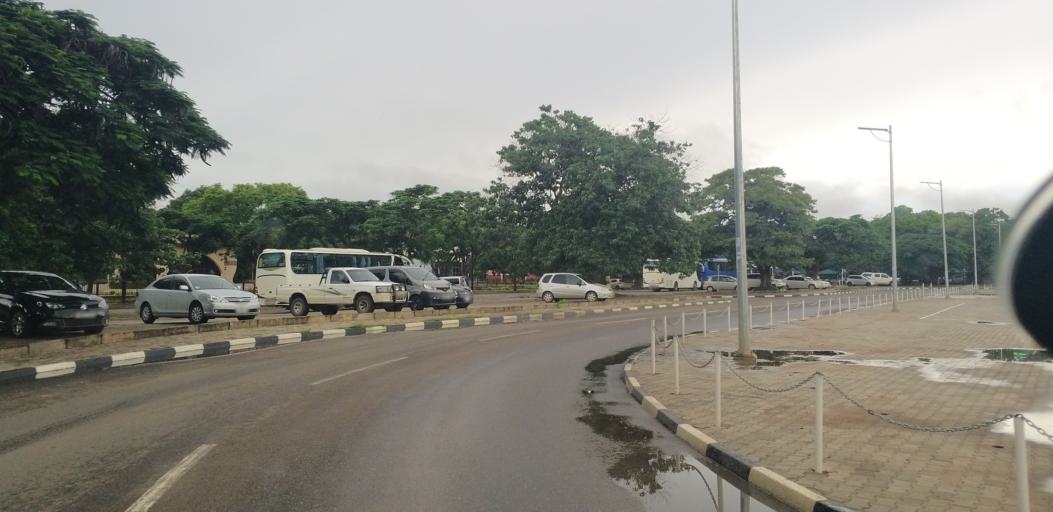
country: ZM
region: Lusaka
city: Lusaka
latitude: -15.4220
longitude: 28.3084
